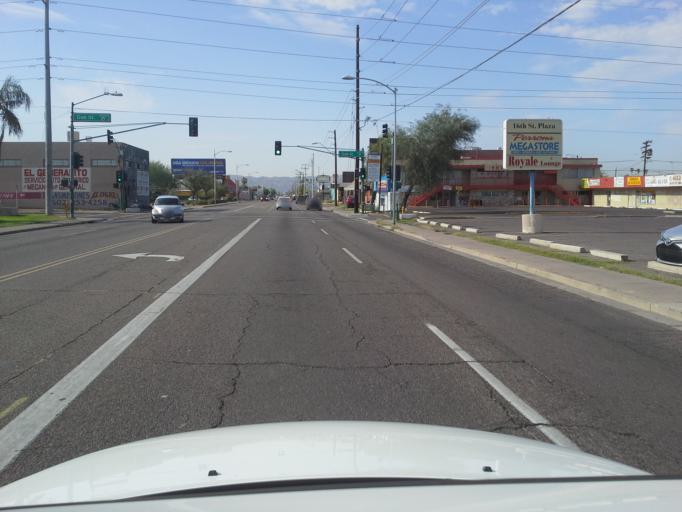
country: US
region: Arizona
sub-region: Maricopa County
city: Phoenix
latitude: 33.4735
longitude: -112.0477
